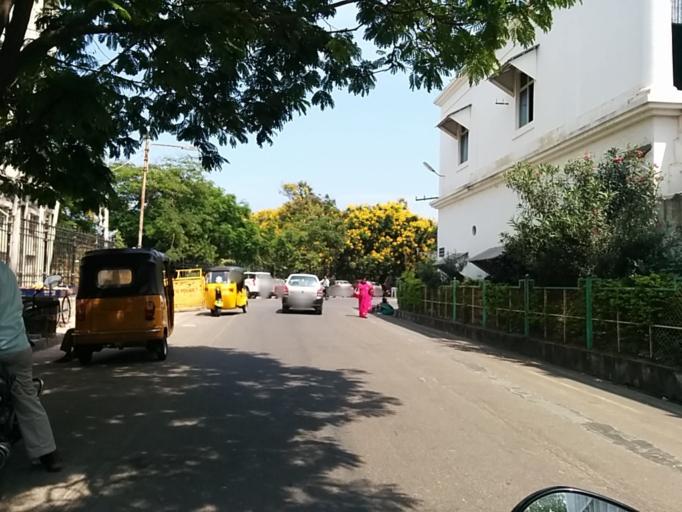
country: IN
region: Pondicherry
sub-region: Puducherry
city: Puducherry
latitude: 11.9326
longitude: 79.8329
